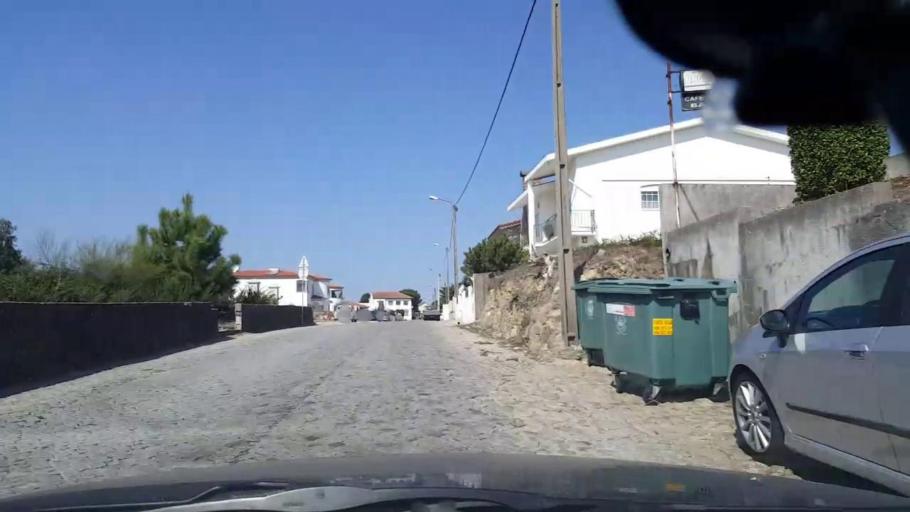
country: PT
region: Porto
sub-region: Vila do Conde
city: Arvore
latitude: 41.3779
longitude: -8.7031
